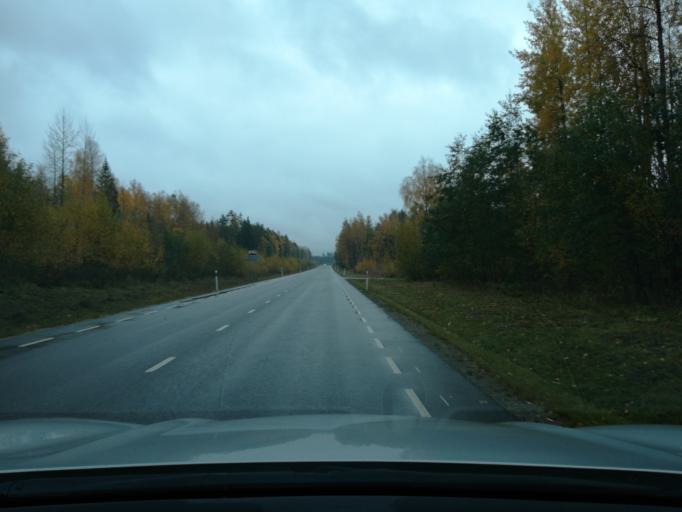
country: EE
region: Ida-Virumaa
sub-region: Johvi vald
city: Johvi
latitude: 59.3068
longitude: 27.4606
